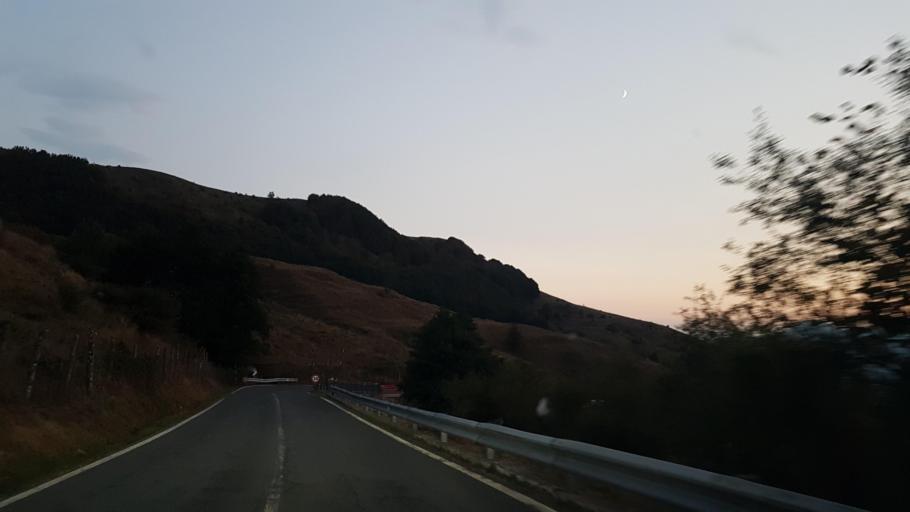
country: IT
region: Liguria
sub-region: Provincia di La Spezia
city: Varese Ligure
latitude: 44.4110
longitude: 9.6291
